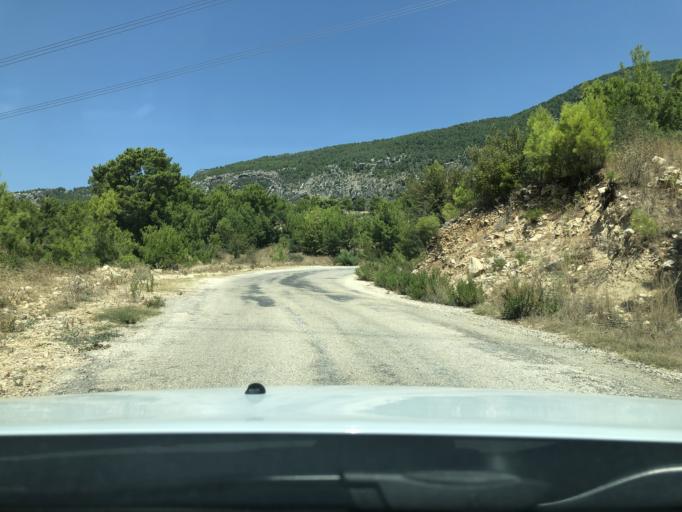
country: TR
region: Antalya
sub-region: Manavgat
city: Manavgat
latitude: 36.8775
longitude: 31.5505
